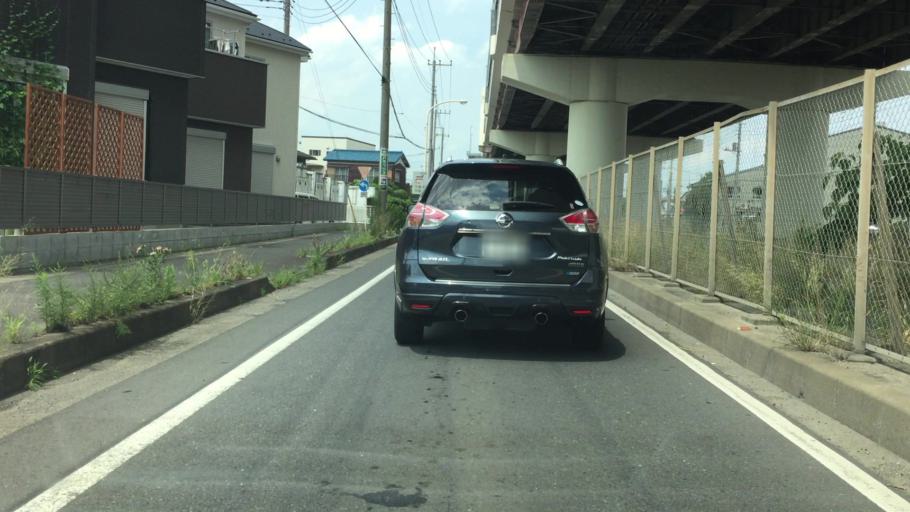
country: JP
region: Saitama
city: Yashio-shi
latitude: 35.8209
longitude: 139.8495
